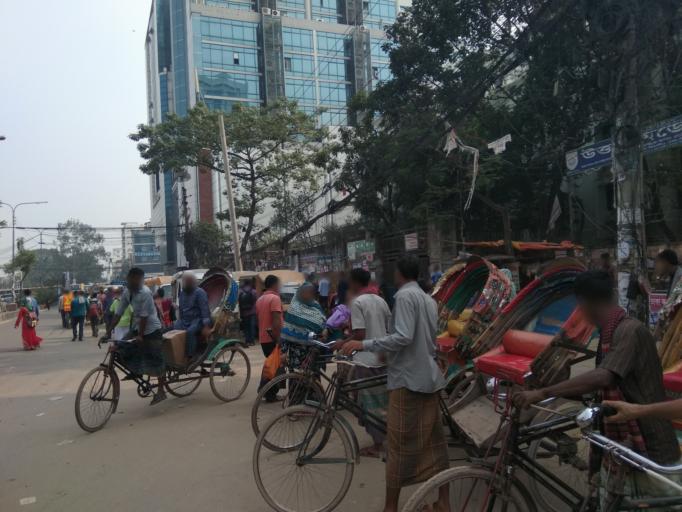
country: BD
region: Dhaka
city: Tungi
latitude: 23.8745
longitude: 90.3992
